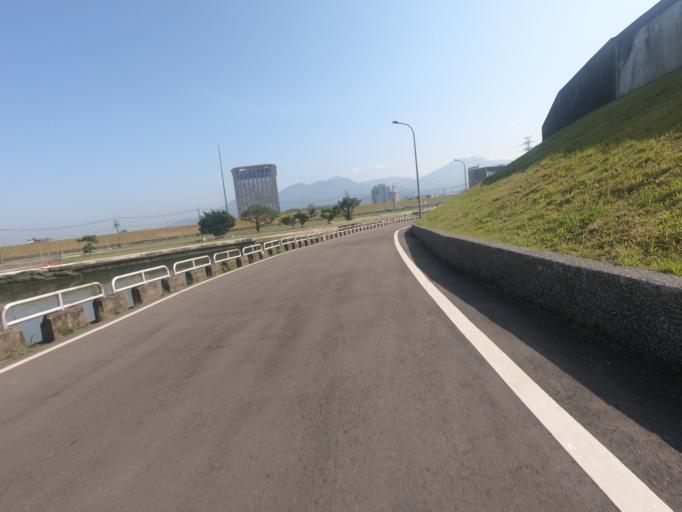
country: TW
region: Taipei
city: Taipei
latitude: 25.0967
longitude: 121.5105
